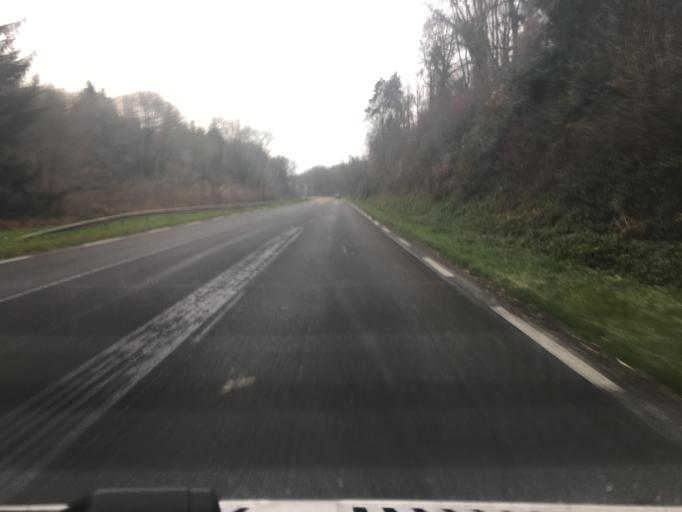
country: FR
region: Haute-Normandie
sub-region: Departement de l'Eure
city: Toutainville
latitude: 49.3852
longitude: 0.4040
